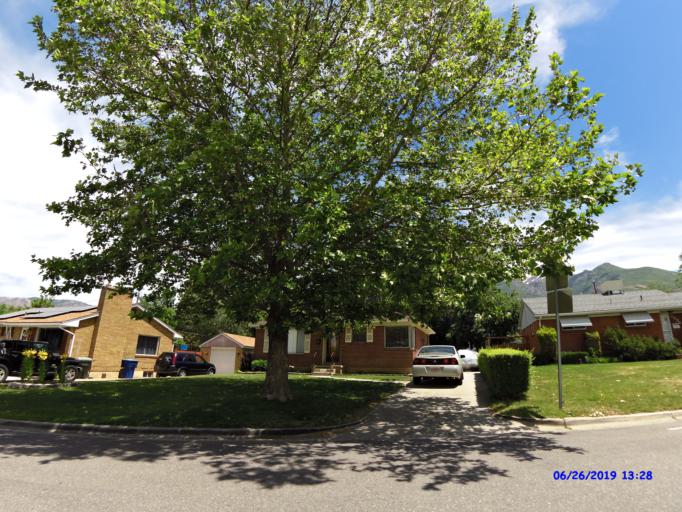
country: US
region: Utah
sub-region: Weber County
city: South Ogden
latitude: 41.2031
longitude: -111.9583
